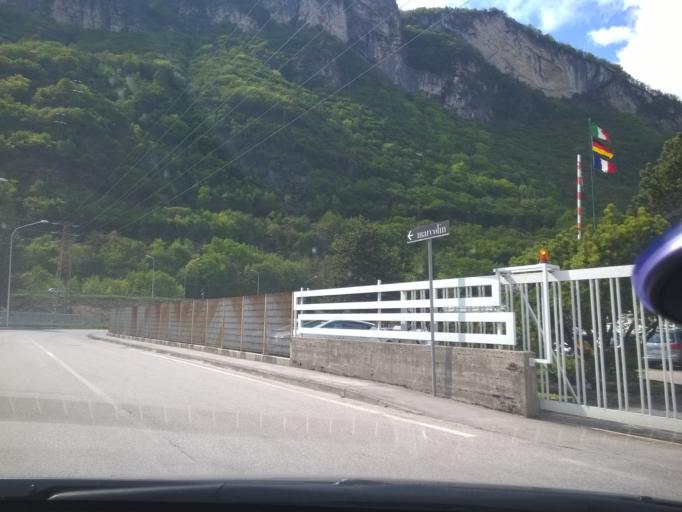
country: IT
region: Veneto
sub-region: Provincia di Belluno
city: Longarone
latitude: 46.2497
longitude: 12.3003
